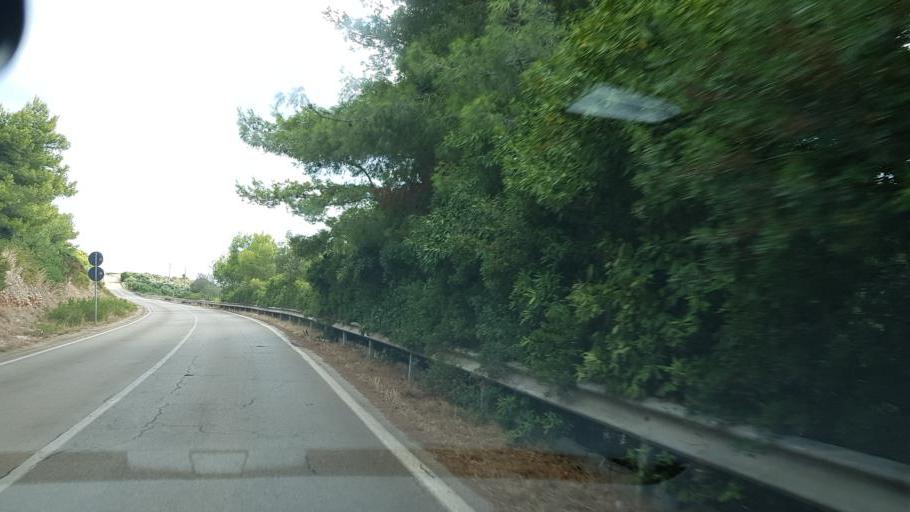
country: IT
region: Apulia
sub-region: Provincia di Lecce
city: Nardo
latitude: 40.1656
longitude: 17.9520
